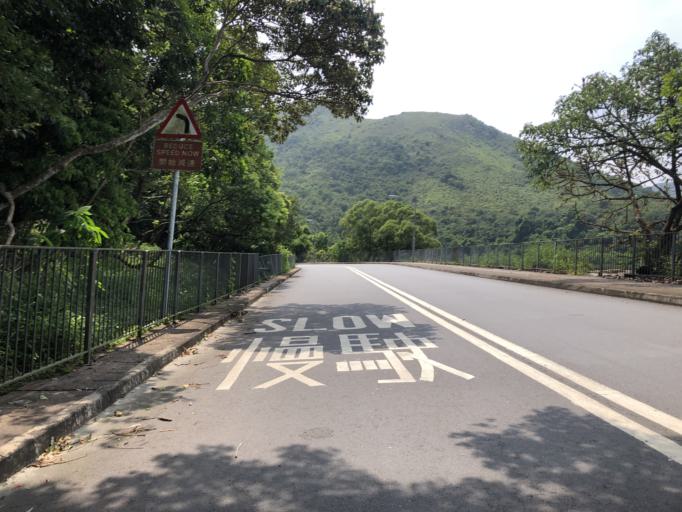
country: CN
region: Guangdong
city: Haishan
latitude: 22.5256
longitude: 114.2110
